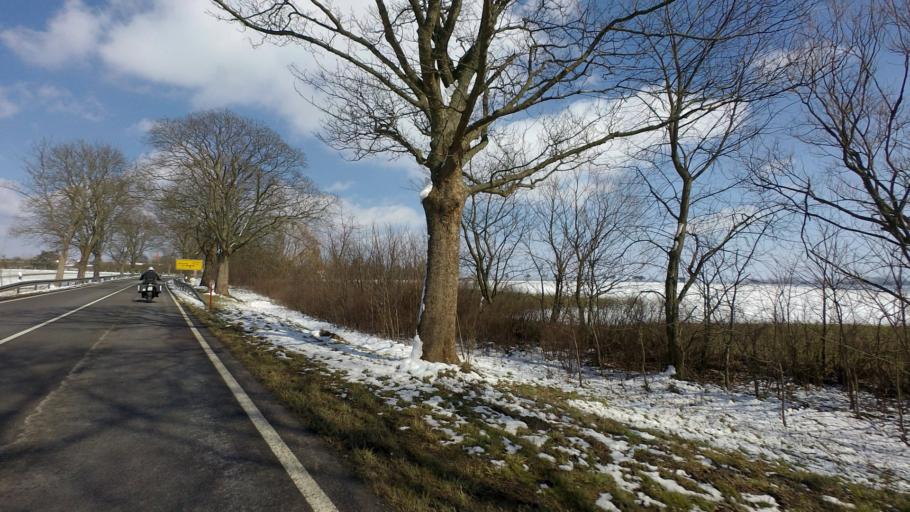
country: DE
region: Brandenburg
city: Werftpfuhl
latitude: 52.7332
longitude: 13.8380
